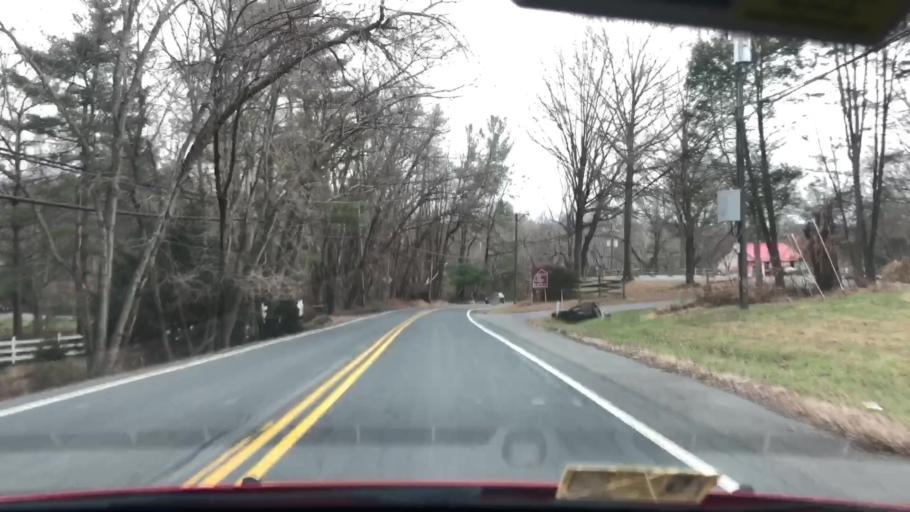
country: US
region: Virginia
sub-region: Fairfax County
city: Great Falls
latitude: 38.9707
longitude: -77.2944
